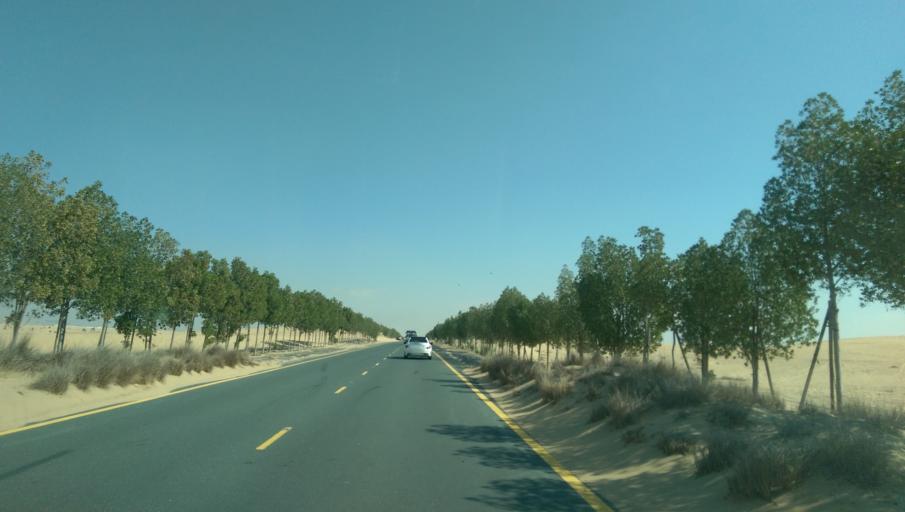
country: AE
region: Dubai
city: Dubai
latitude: 24.9809
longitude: 55.3406
